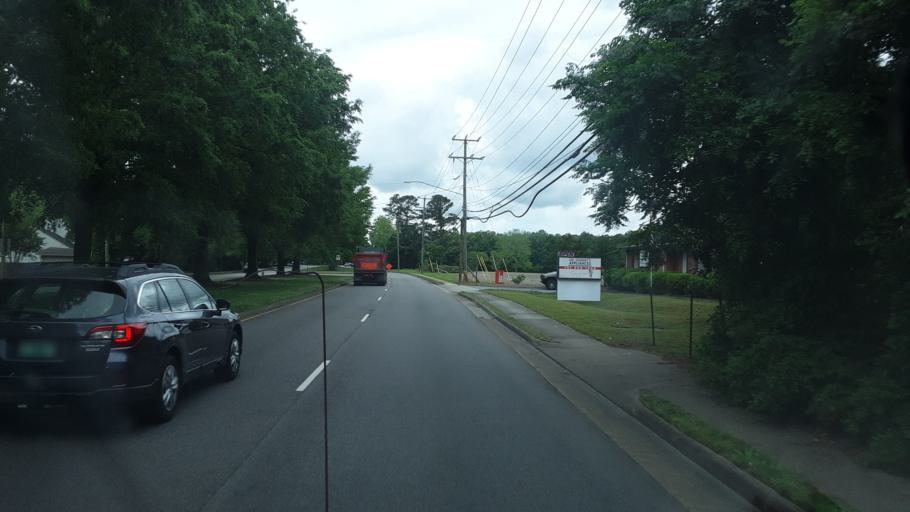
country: US
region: Virginia
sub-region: City of Virginia Beach
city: Virginia Beach
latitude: 36.7740
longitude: -76.0084
